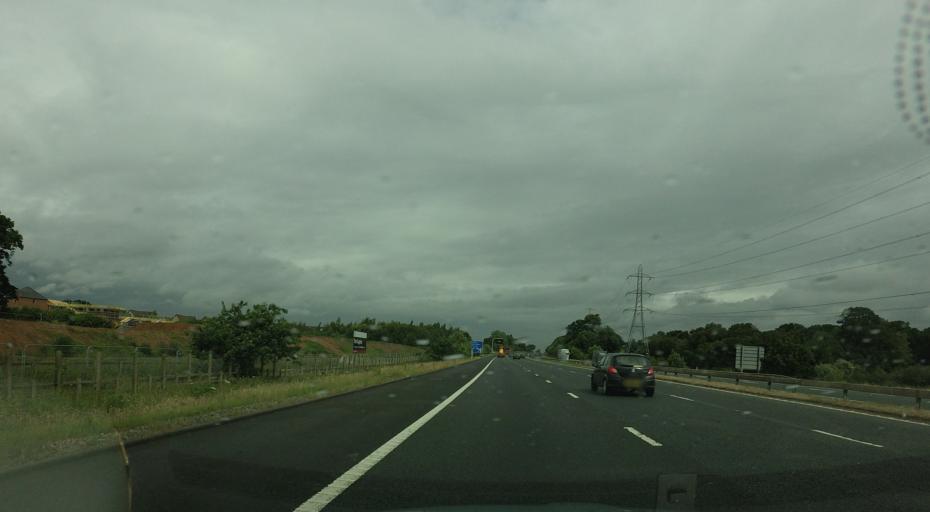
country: GB
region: England
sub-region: Cumbria
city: Scotby
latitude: 54.8760
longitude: -2.8786
